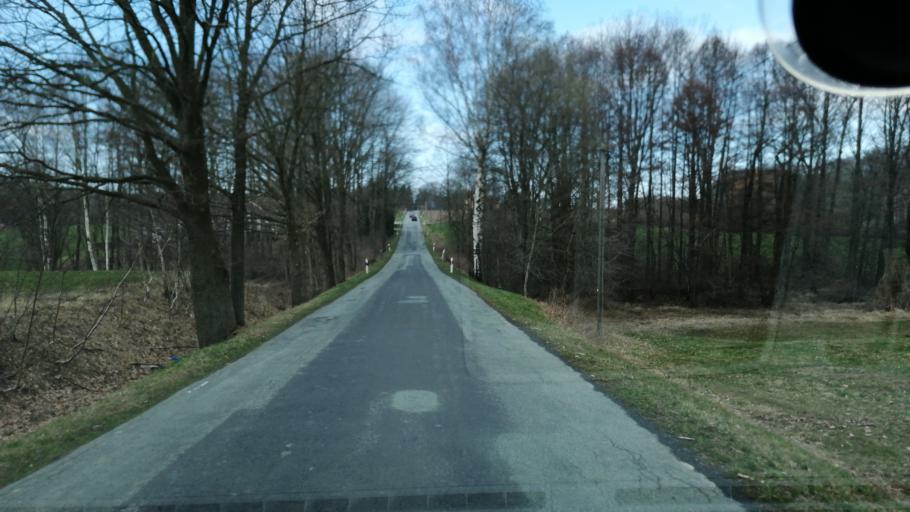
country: DE
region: Saxony
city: Herrnhut
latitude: 51.0273
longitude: 14.7078
